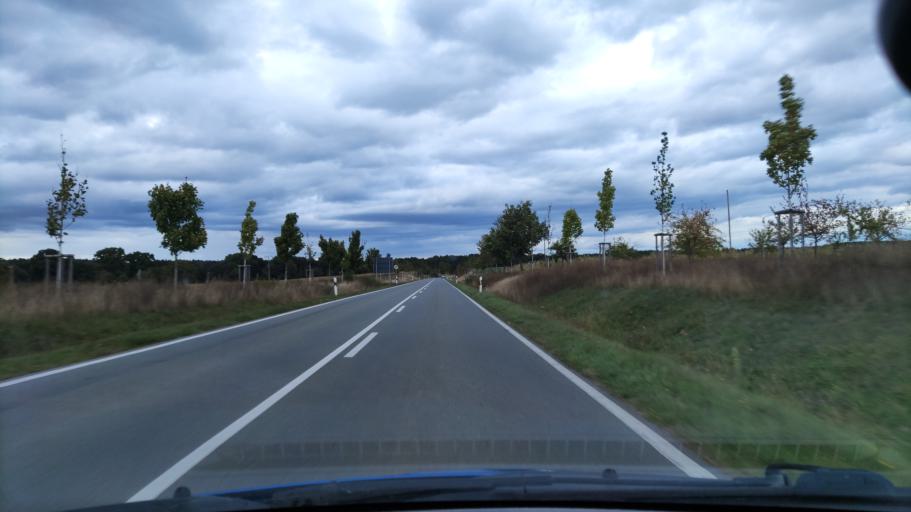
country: DE
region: Mecklenburg-Vorpommern
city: Lubtheen
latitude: 53.3671
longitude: 10.9640
